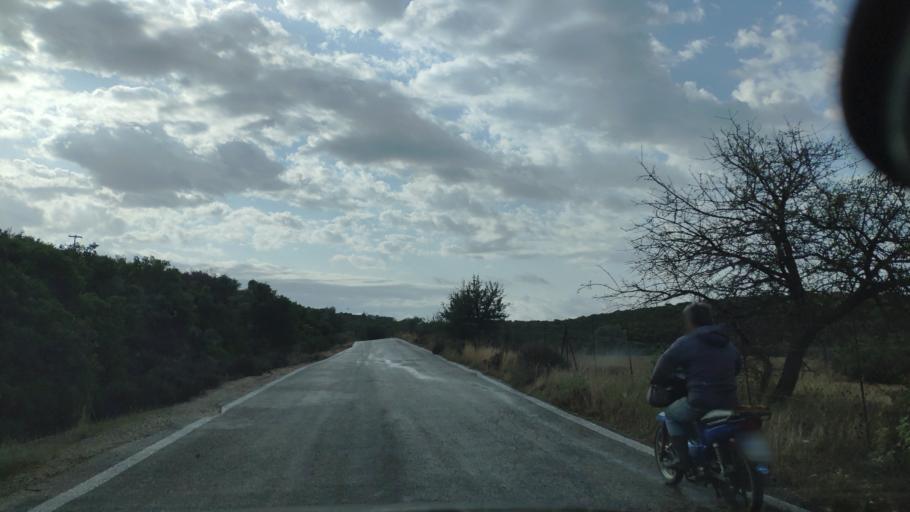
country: GR
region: West Greece
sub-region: Nomos Aitolias kai Akarnanias
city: Sardinia
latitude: 38.8831
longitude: 21.2452
